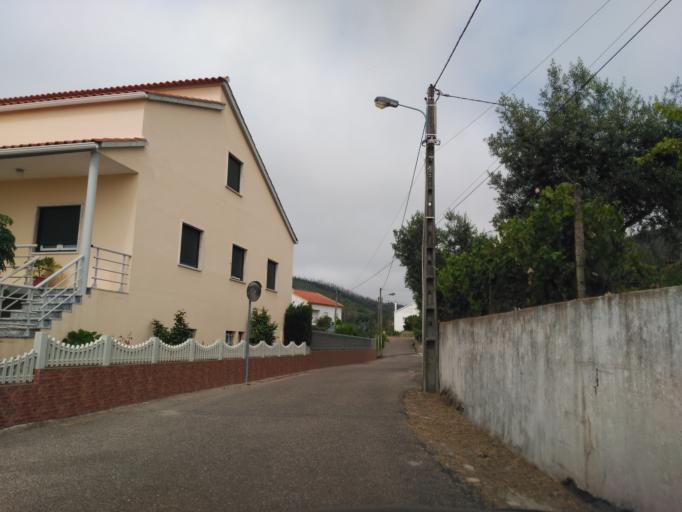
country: PT
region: Santarem
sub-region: Macao
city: Macao
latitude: 39.5869
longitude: -8.0589
